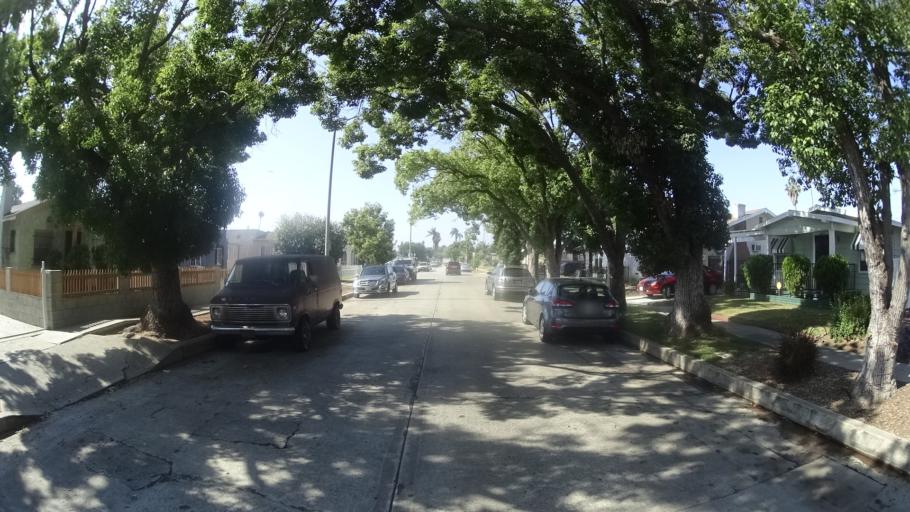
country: US
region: California
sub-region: Los Angeles County
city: View Park-Windsor Hills
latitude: 33.9788
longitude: -118.3225
